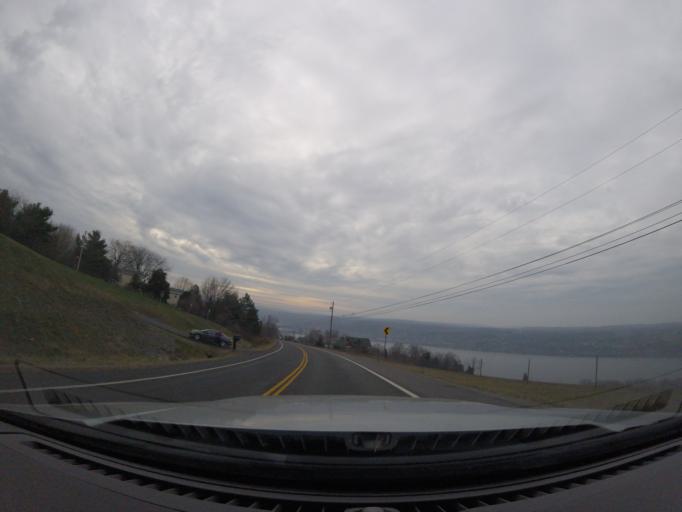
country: US
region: New York
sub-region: Schuyler County
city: Watkins Glen
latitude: 42.4046
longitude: -76.8572
